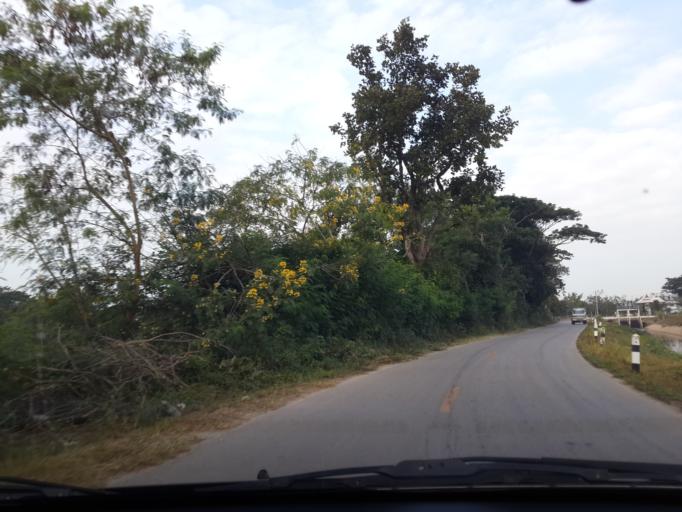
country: TH
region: Chiang Mai
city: San Sai
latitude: 18.8948
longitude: 99.0585
